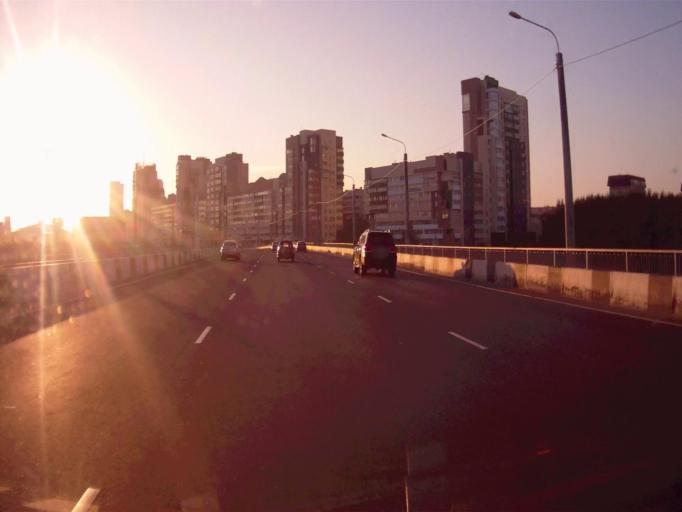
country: RU
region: Chelyabinsk
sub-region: Gorod Chelyabinsk
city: Chelyabinsk
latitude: 55.1730
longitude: 61.4087
